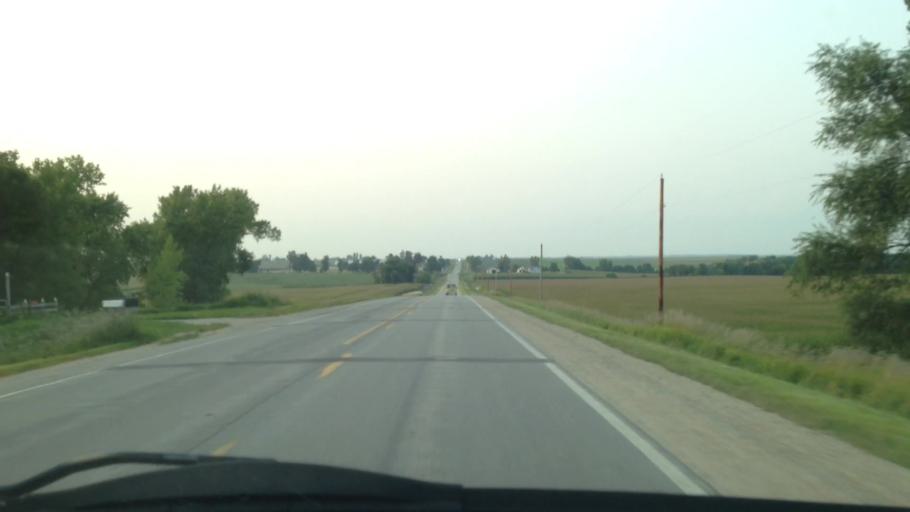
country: US
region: Iowa
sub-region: Benton County
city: Atkins
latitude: 41.9981
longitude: -91.8734
